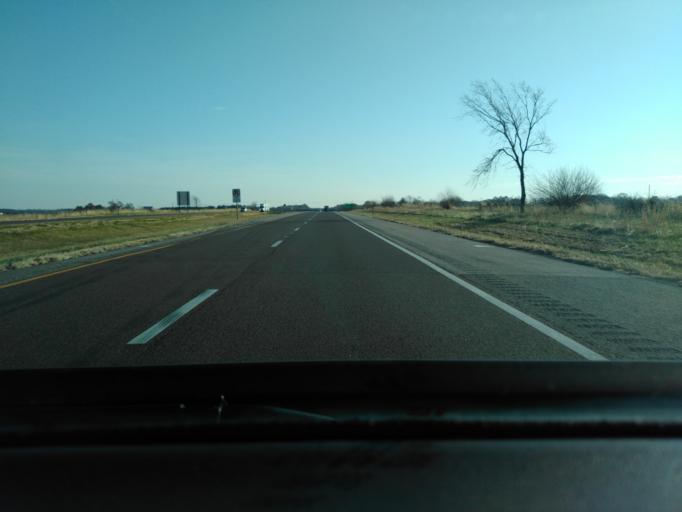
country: US
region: Illinois
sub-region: Madison County
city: Saint Jacob
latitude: 38.7628
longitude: -89.7877
